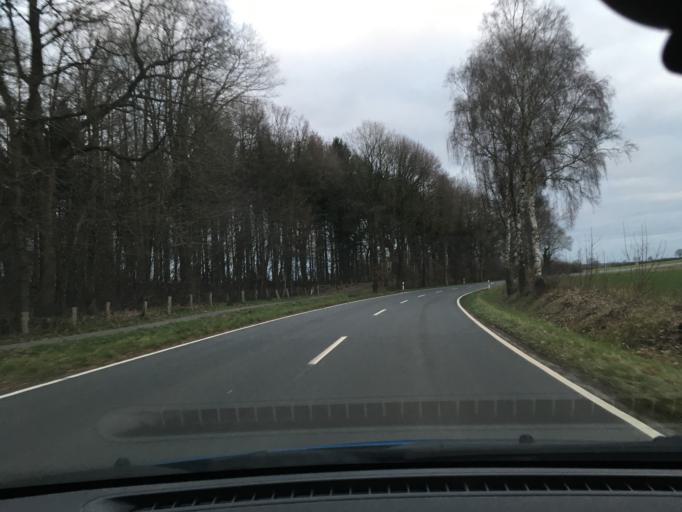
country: DE
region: Schleswig-Holstein
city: Mehlbek
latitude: 53.9964
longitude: 9.4415
